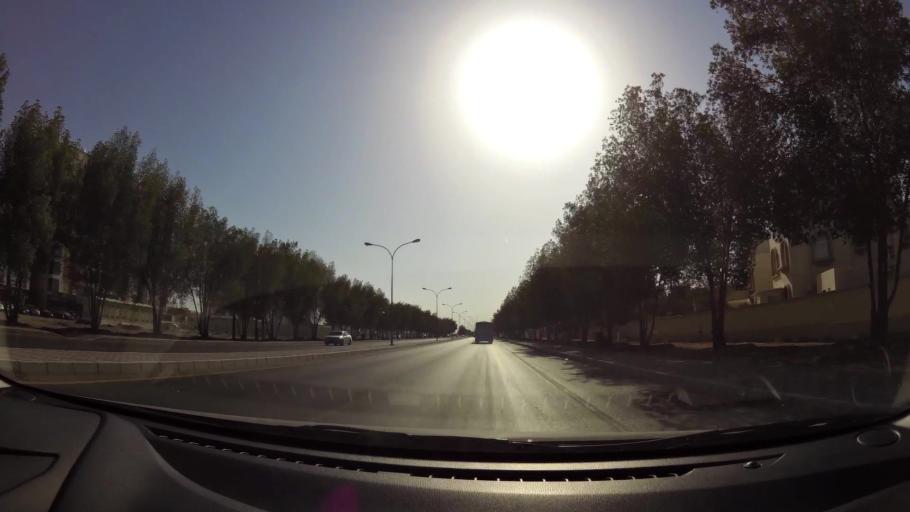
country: OM
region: Muhafazat Masqat
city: As Sib al Jadidah
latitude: 23.6163
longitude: 58.1985
